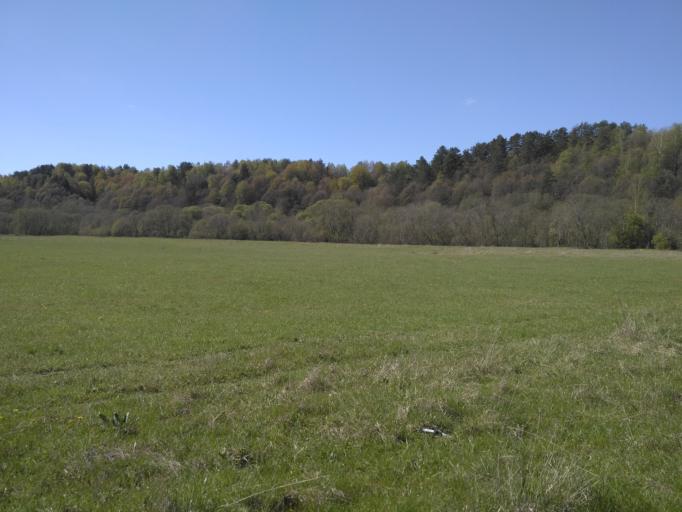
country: BY
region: Mogilev
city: Mstsislaw
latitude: 54.0449
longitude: 31.7040
